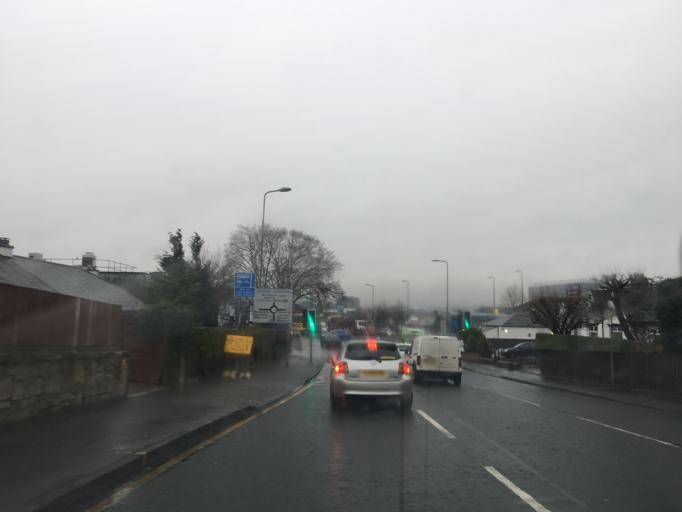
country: GB
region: Scotland
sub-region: Edinburgh
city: Currie
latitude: 55.9435
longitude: -3.2935
